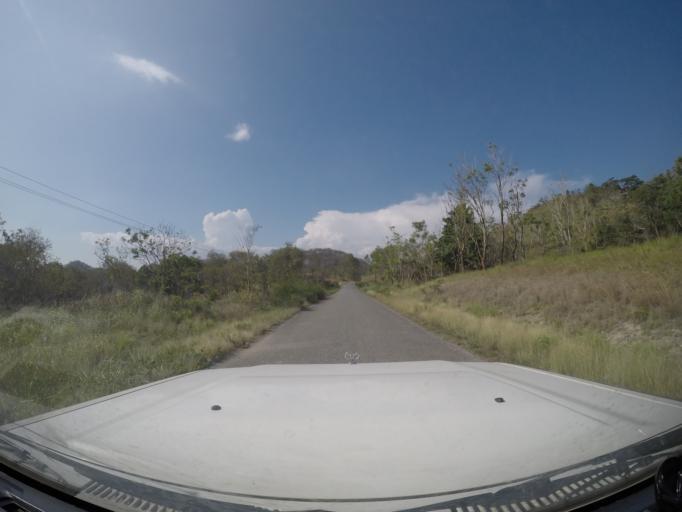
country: PG
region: Central Province
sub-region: Rigo
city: Kwikila
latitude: -9.8613
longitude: 147.5630
